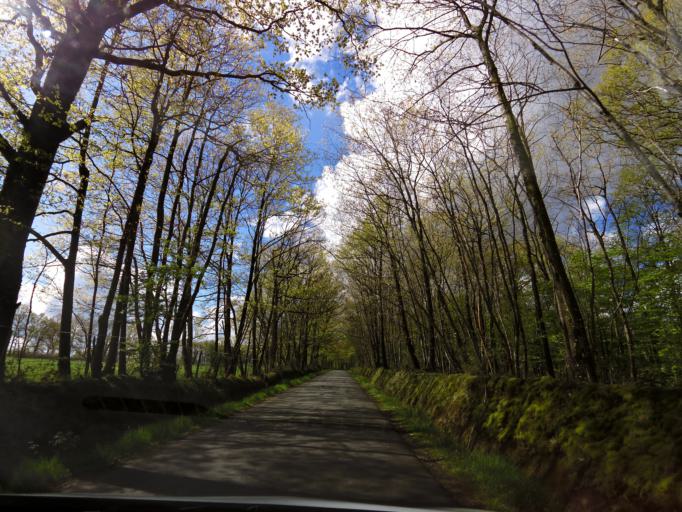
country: FR
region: Brittany
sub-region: Departement d'Ille-et-Vilaine
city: Orgeres
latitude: 47.9709
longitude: -1.6761
